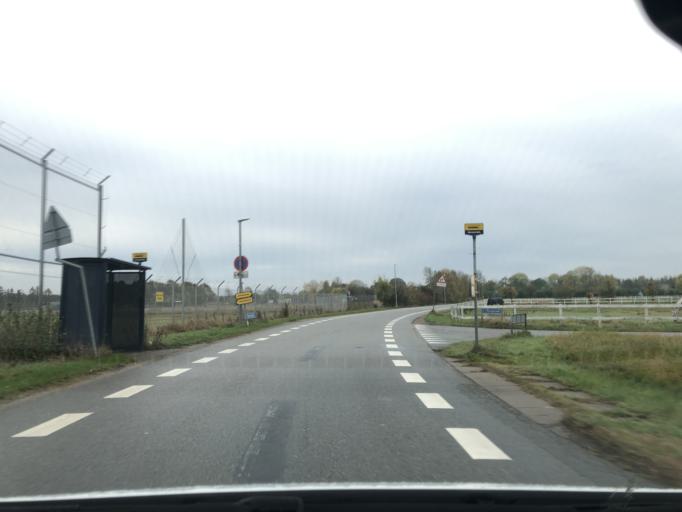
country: DK
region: Capital Region
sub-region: Tarnby Kommune
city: Tarnby
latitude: 55.5870
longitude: 12.5990
